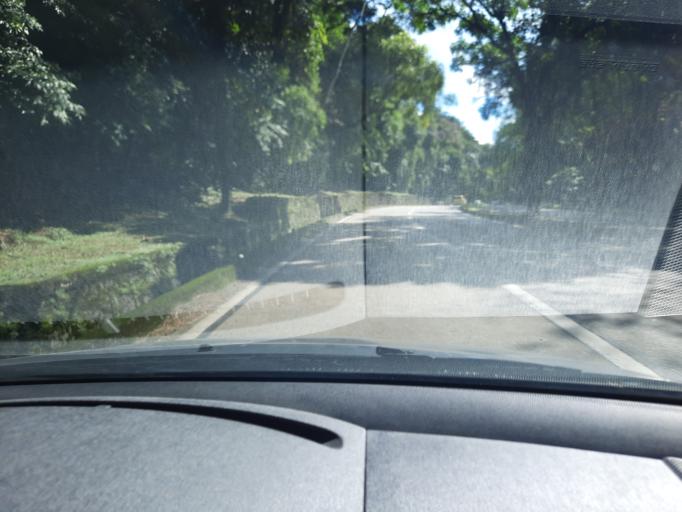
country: BR
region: Rio de Janeiro
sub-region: Petropolis
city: Petropolis
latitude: -22.5621
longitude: -43.2289
